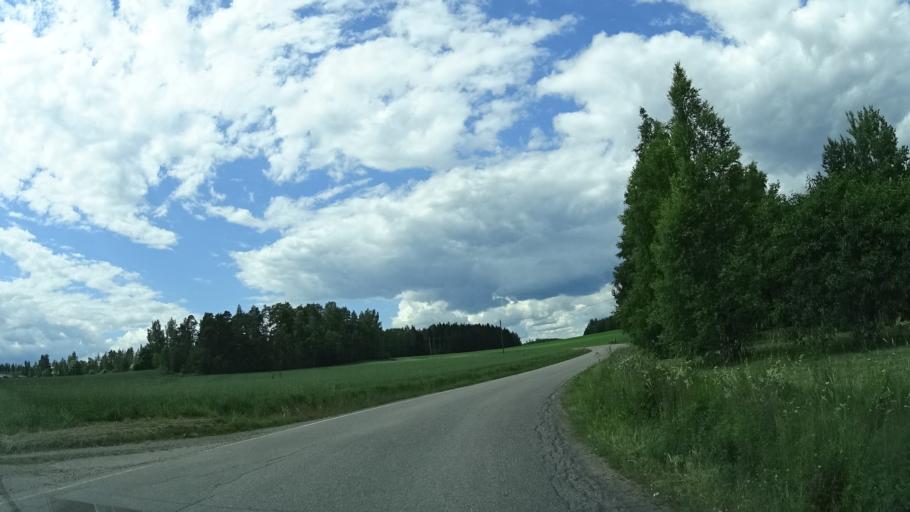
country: FI
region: Uusimaa
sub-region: Helsinki
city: Nurmijaervi
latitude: 60.4013
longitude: 24.6275
